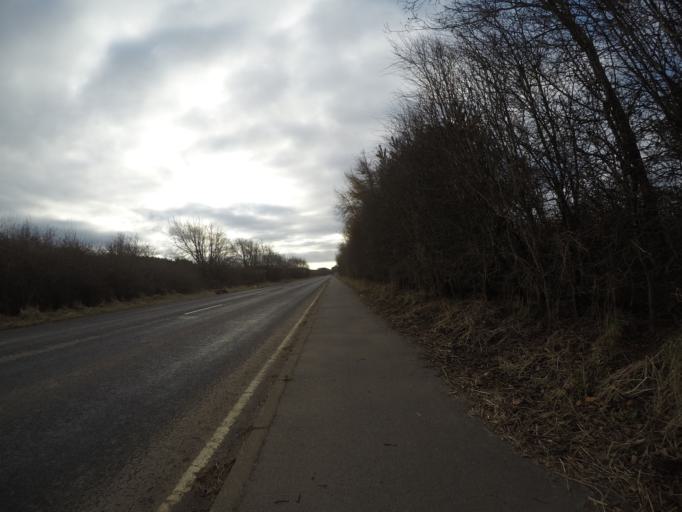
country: GB
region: Scotland
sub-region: North Ayrshire
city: Irvine
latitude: 55.5890
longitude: -4.6499
